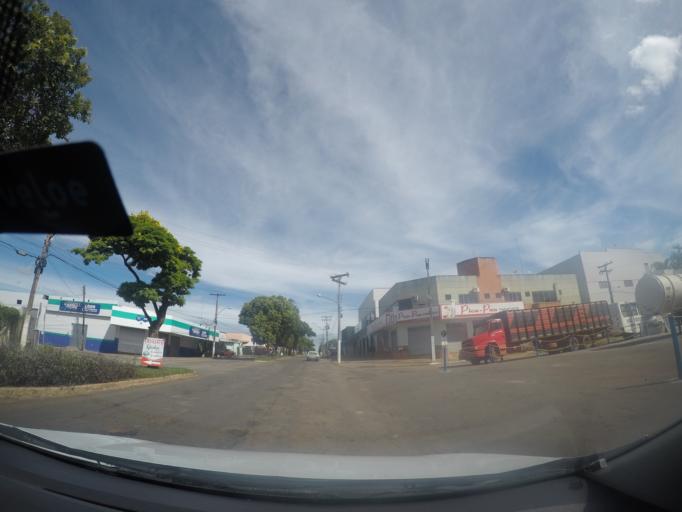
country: BR
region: Goias
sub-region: Inhumas
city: Inhumas
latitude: -16.3701
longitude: -49.4940
